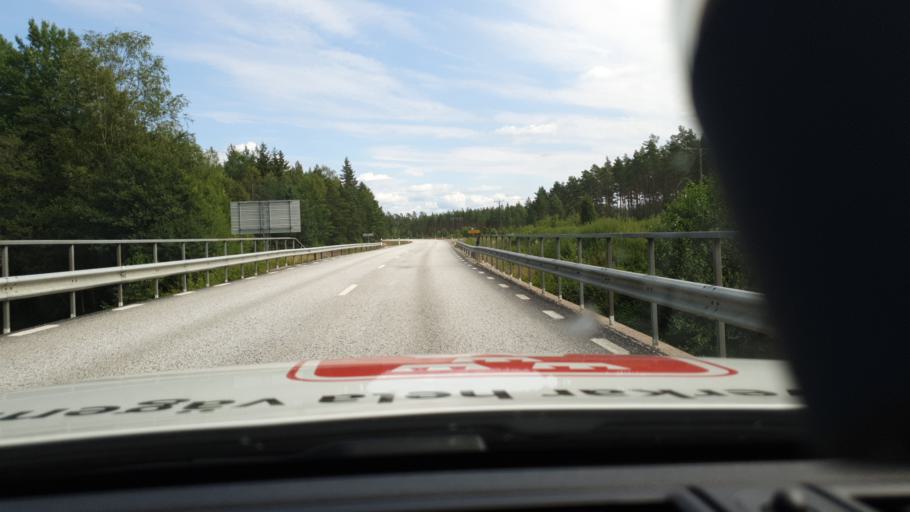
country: SE
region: Joenkoeping
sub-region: Gnosjo Kommun
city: Hillerstorp
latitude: 57.2973
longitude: 13.8656
